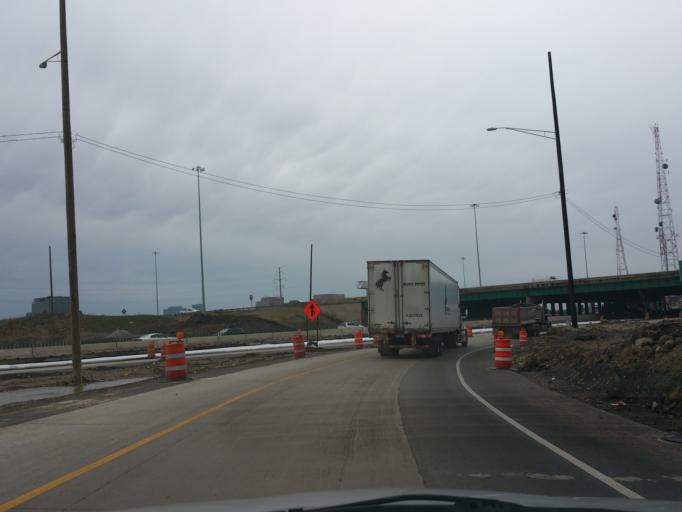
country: US
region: Illinois
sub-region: Cook County
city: Rolling Meadows
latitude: 42.0579
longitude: -88.0262
